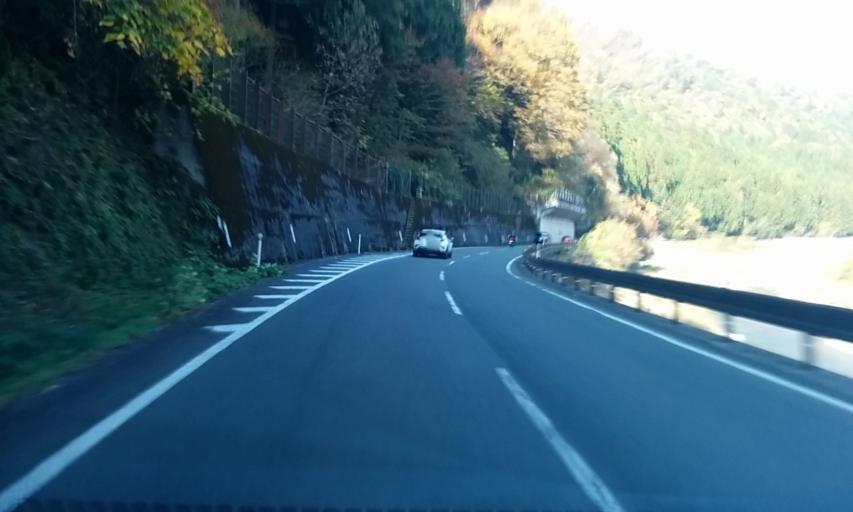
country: JP
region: Fukui
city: Obama
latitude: 35.2991
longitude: 135.6146
